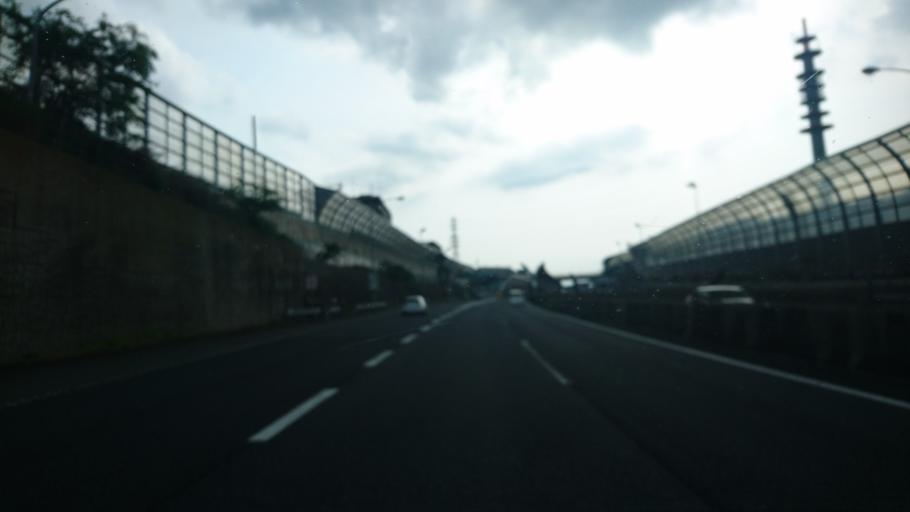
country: JP
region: Kanagawa
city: Yokohama
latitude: 35.4535
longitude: 139.5790
